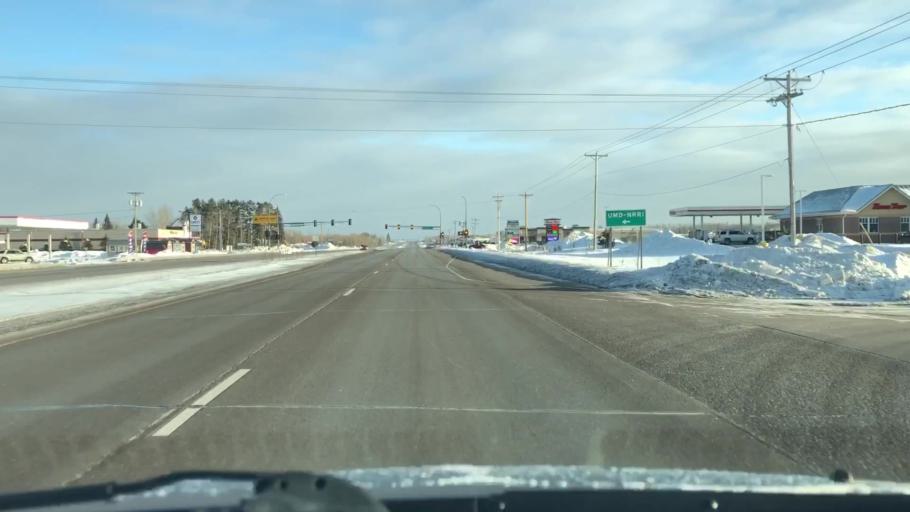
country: US
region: Minnesota
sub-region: Saint Louis County
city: Hermantown
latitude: 46.8347
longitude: -92.2075
